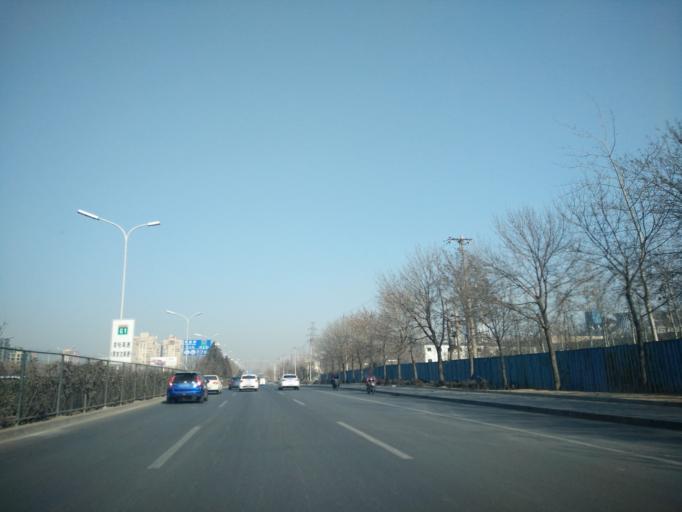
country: CN
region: Beijing
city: Longtan
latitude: 39.8612
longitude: 116.4817
